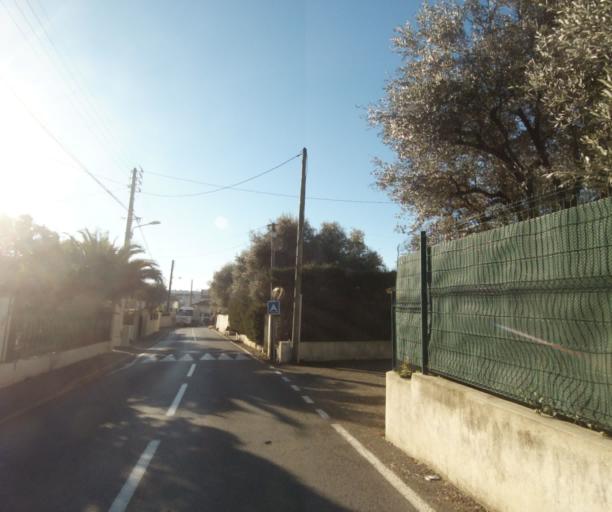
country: FR
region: Provence-Alpes-Cote d'Azur
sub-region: Departement des Alpes-Maritimes
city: Antibes
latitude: 43.5798
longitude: 7.1054
